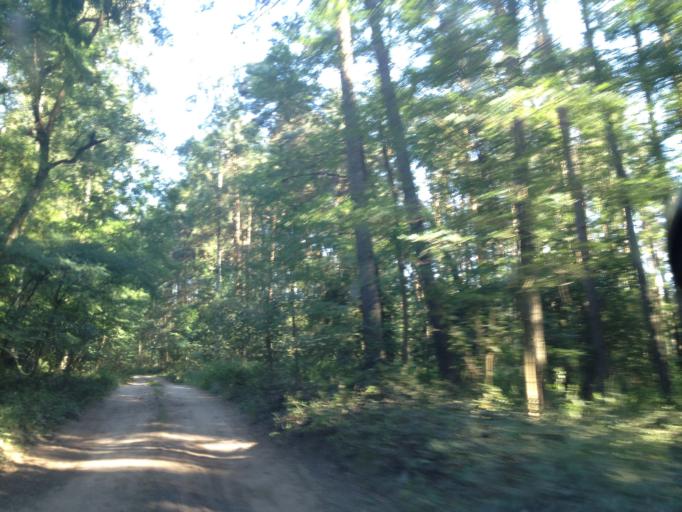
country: PL
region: Greater Poland Voivodeship
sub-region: Powiat sredzki
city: Zaniemysl
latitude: 52.1063
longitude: 17.1285
